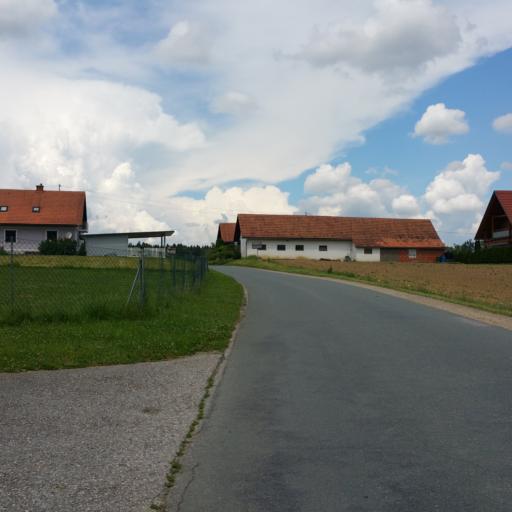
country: AT
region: Styria
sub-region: Politischer Bezirk Leibnitz
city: Gleinstatten
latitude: 46.7457
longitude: 15.3514
